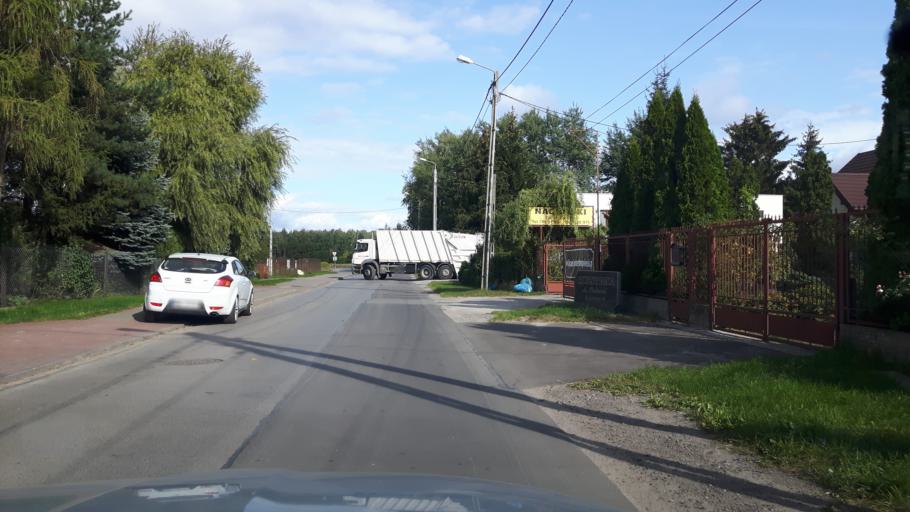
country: PL
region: Masovian Voivodeship
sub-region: Powiat wolominski
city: Marki
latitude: 52.3321
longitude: 21.0918
